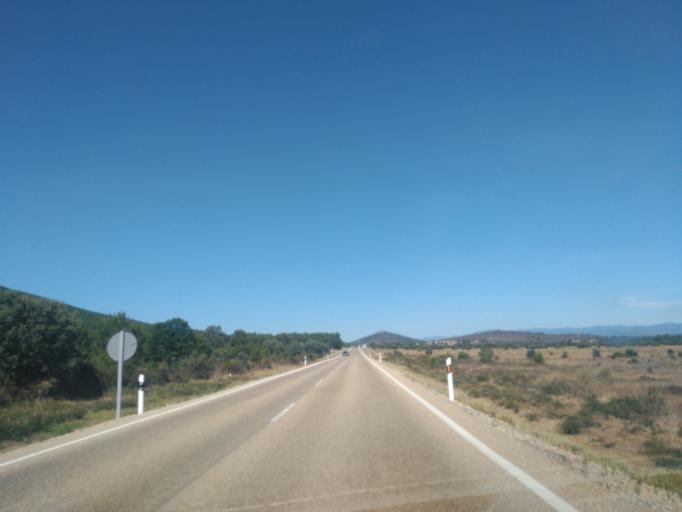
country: ES
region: Castille and Leon
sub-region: Provincia de Zamora
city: Ferreras de Abajo
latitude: 41.9259
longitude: -6.1043
